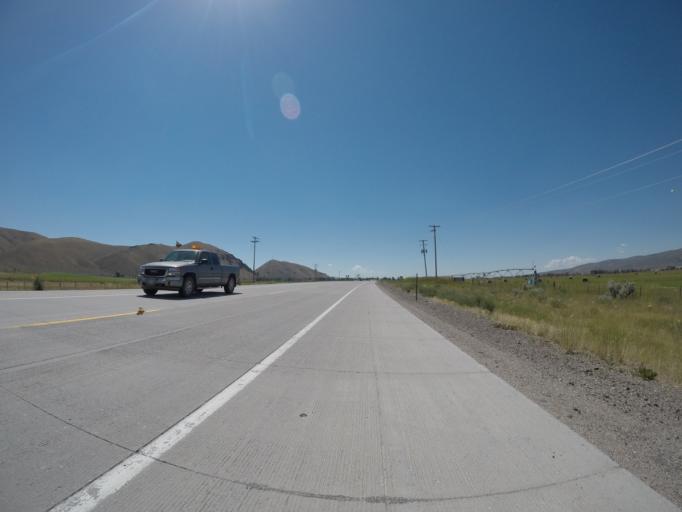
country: US
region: Idaho
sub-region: Bear Lake County
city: Montpelier
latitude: 42.1104
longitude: -110.9559
